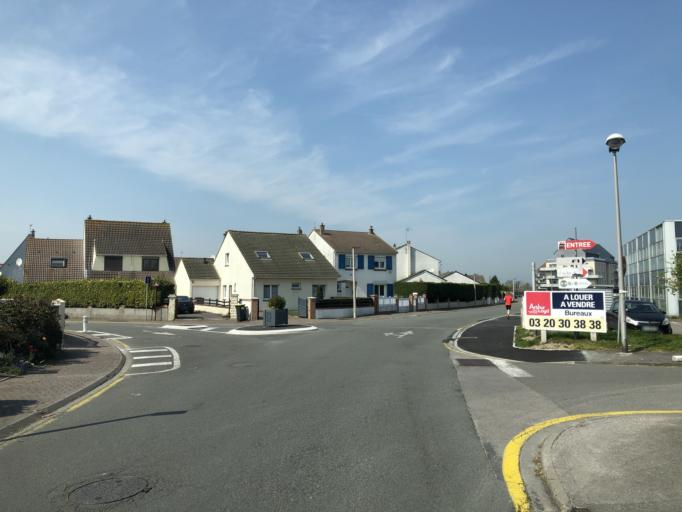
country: FR
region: Nord-Pas-de-Calais
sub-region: Departement du Pas-de-Calais
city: Coquelles
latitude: 50.9415
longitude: 1.8027
